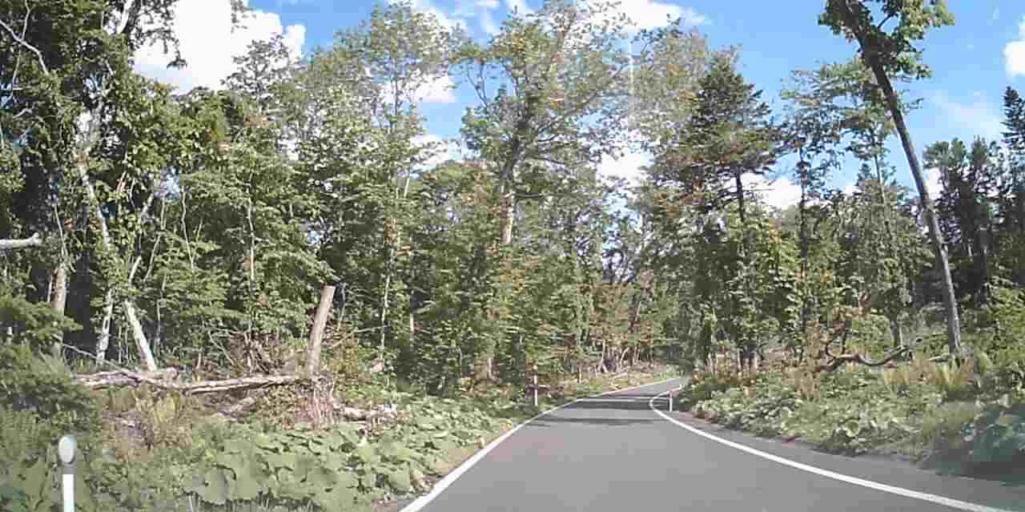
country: JP
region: Hokkaido
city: Shiraoi
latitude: 42.7327
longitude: 141.4111
